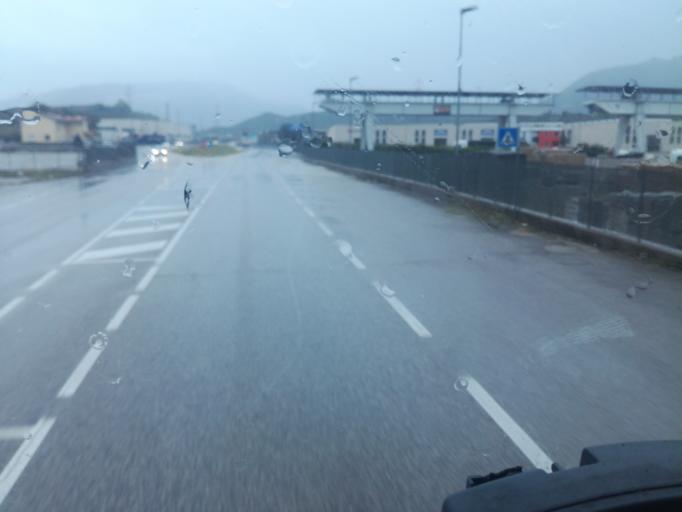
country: IT
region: Veneto
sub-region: Provincia di Verona
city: Volargne
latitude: 45.5397
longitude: 10.8018
